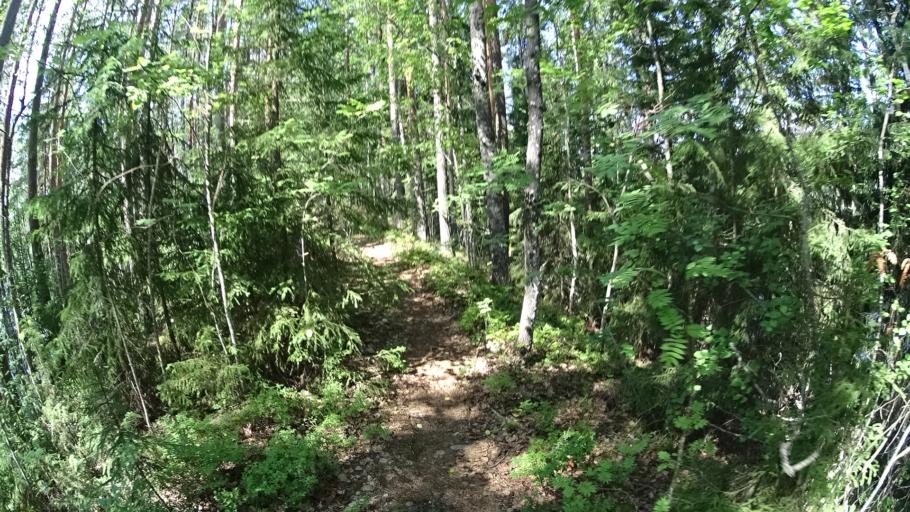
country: FI
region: Haeme
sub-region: Forssa
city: Tammela
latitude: 60.7715
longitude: 23.8572
